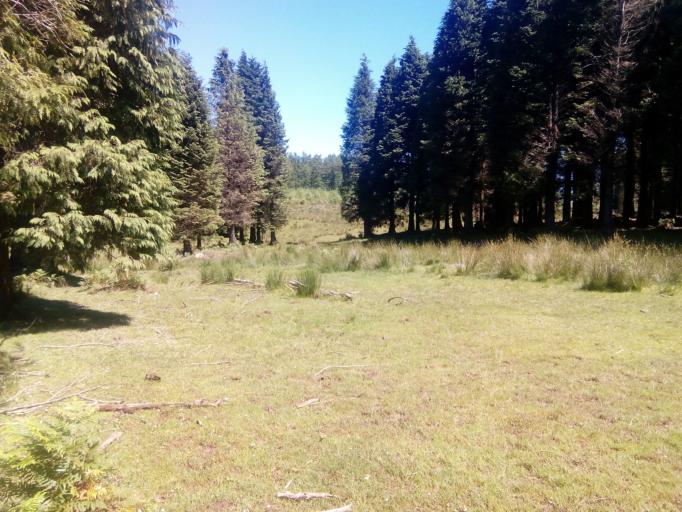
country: ES
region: Basque Country
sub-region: Provincia de Guipuzcoa
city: Urnieta
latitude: 43.1979
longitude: -1.9770
